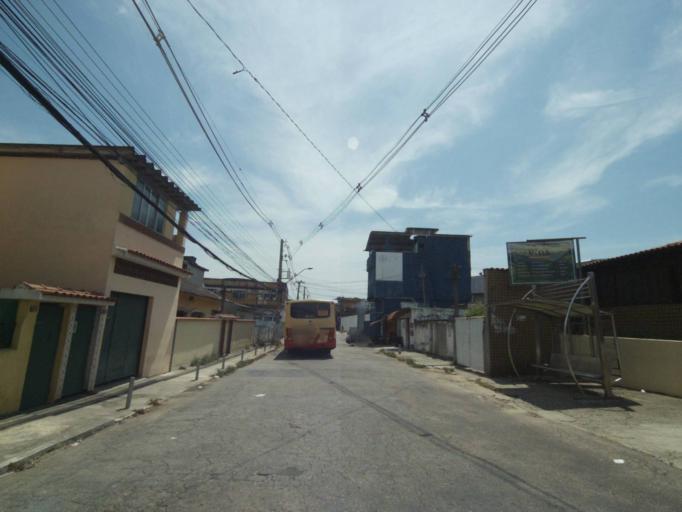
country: BR
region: Rio de Janeiro
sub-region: Duque De Caxias
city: Duque de Caxias
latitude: -22.7970
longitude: -43.2915
